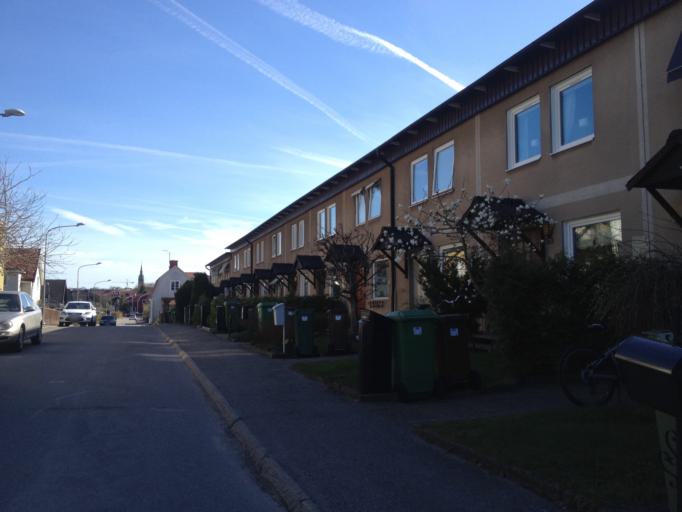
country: SE
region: OEstergoetland
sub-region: Norrkopings Kommun
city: Norrkoping
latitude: 58.6027
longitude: 16.1697
